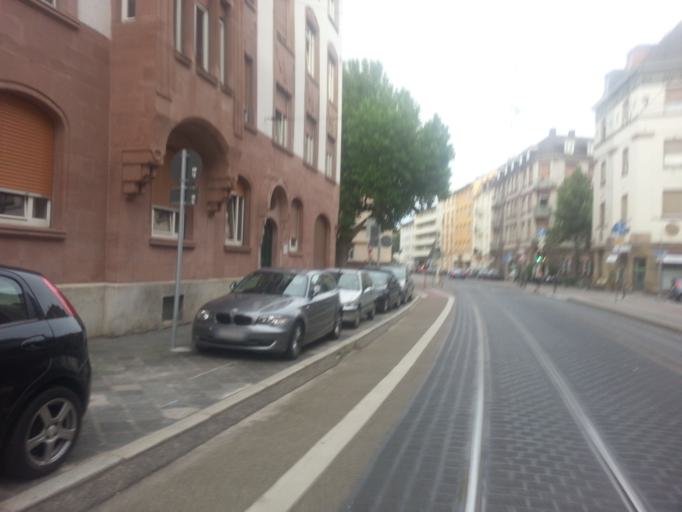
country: DE
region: Baden-Wuerttemberg
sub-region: Karlsruhe Region
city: Mannheim
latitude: 49.4767
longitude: 8.4853
